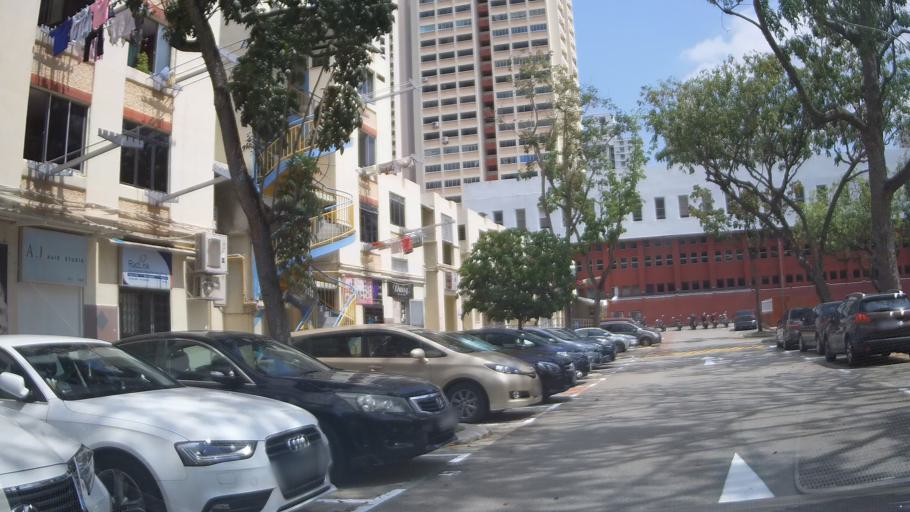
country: SG
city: Singapore
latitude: 1.3327
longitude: 103.8504
